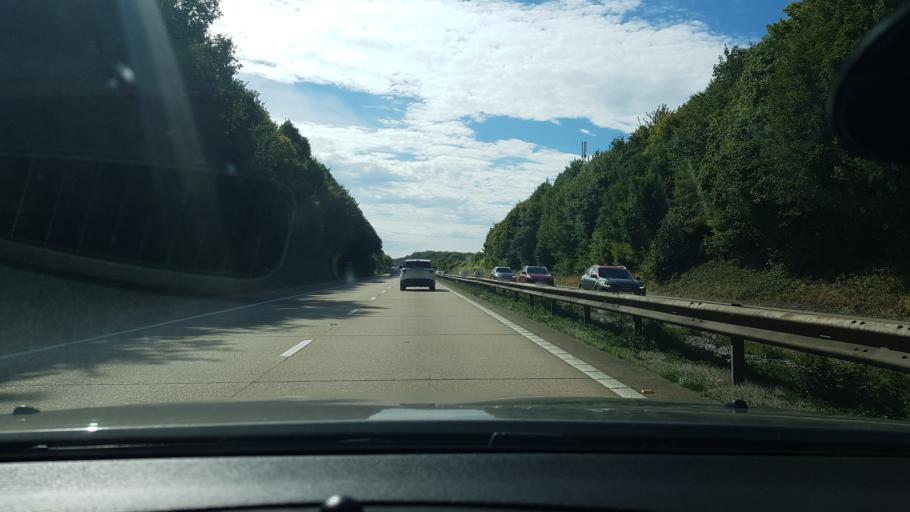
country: GB
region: England
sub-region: Hampshire
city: Kings Worthy
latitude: 51.1552
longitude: -1.2376
